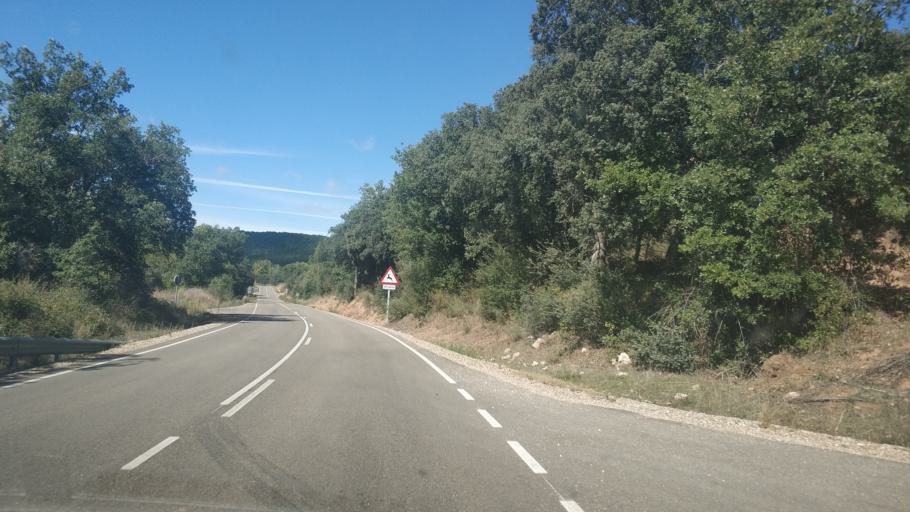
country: ES
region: Castille and Leon
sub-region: Provincia de Burgos
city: Puentedura
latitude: 42.0521
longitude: -3.5524
